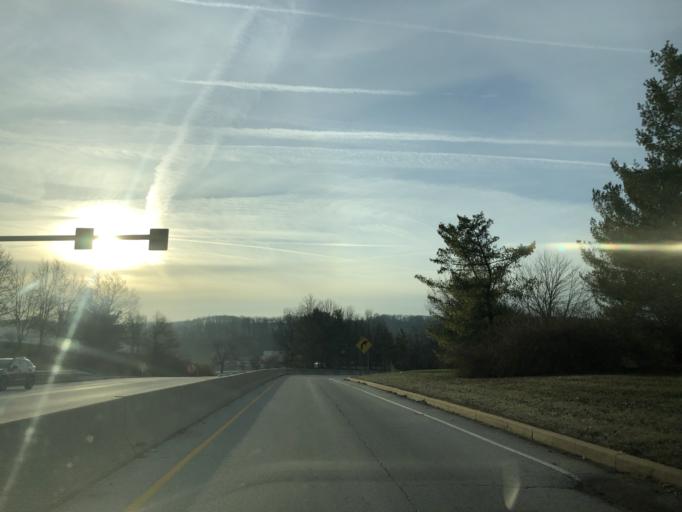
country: US
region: Pennsylvania
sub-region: Chester County
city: Malvern
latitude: 40.0538
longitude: -75.5205
